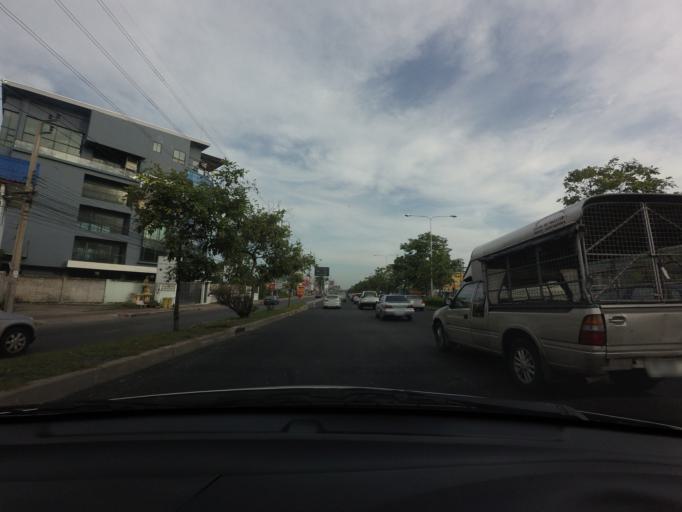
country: TH
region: Nonthaburi
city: Bang Kruai
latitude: 13.8169
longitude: 100.4494
